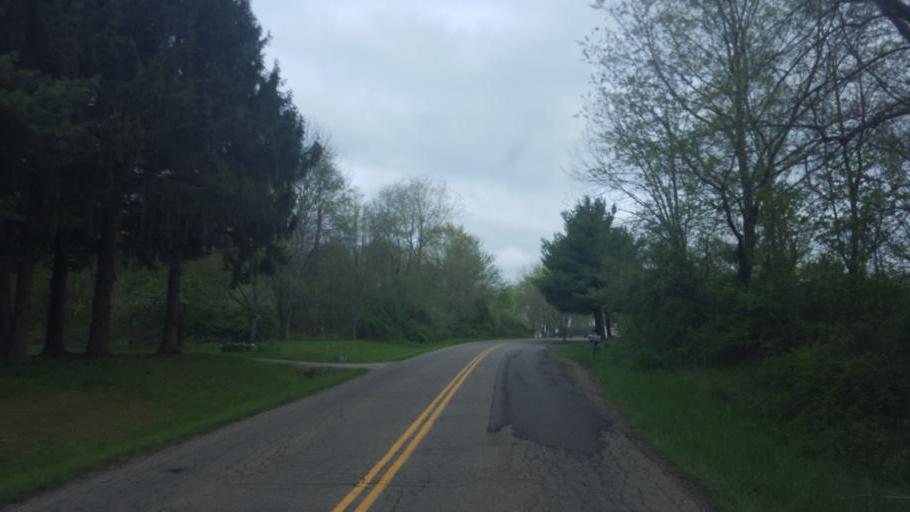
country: US
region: Ohio
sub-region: Knox County
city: Gambier
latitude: 40.4176
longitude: -82.3646
